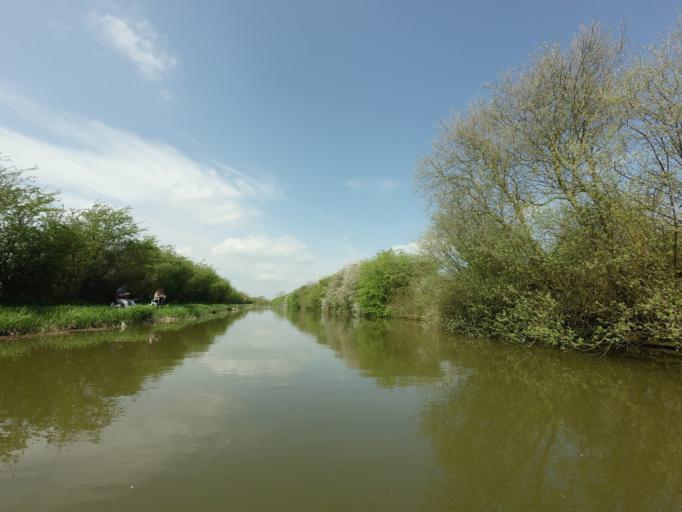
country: GB
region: England
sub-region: Buckinghamshire
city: Cheddington
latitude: 51.8761
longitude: -0.6557
